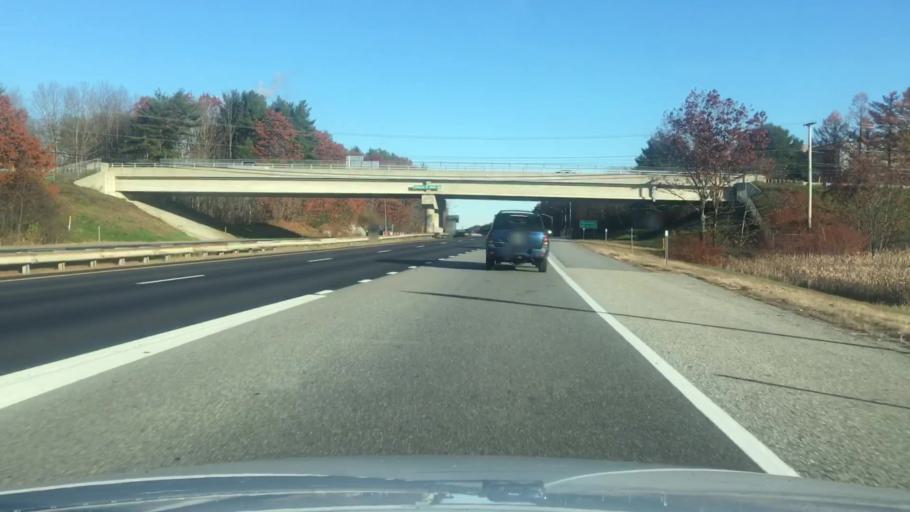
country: US
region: Maine
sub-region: Cumberland County
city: South Portland Gardens
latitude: 43.6500
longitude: -70.3311
